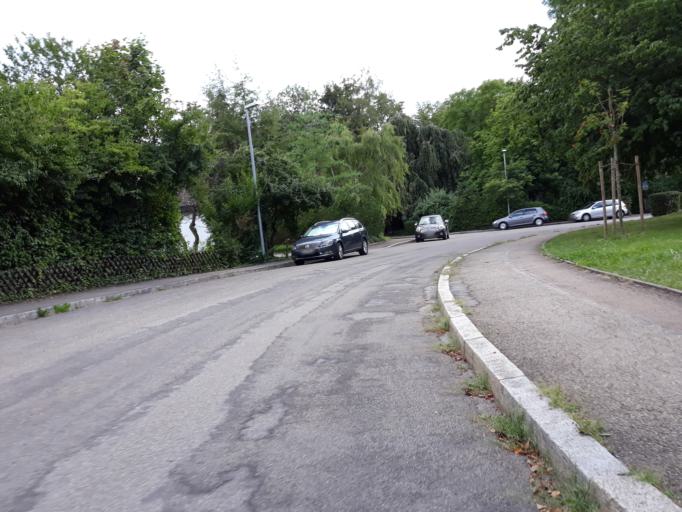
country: DE
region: Baden-Wuerttemberg
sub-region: Regierungsbezirk Stuttgart
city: Schonaich
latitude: 48.6686
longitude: 9.0495
